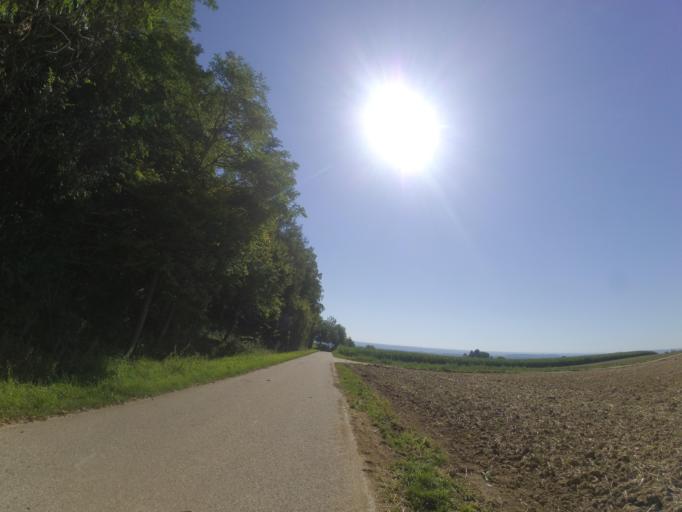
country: DE
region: Bavaria
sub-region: Swabia
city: Nersingen
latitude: 48.4511
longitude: 10.0658
